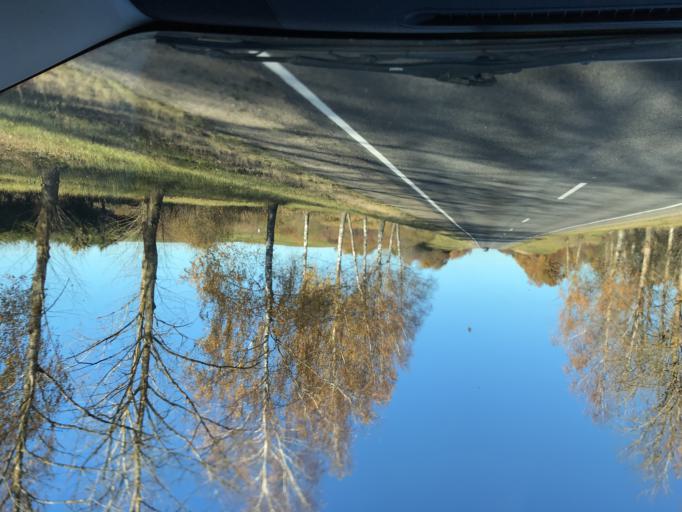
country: BY
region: Vitebsk
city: Lyepyel'
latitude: 55.0173
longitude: 28.7419
